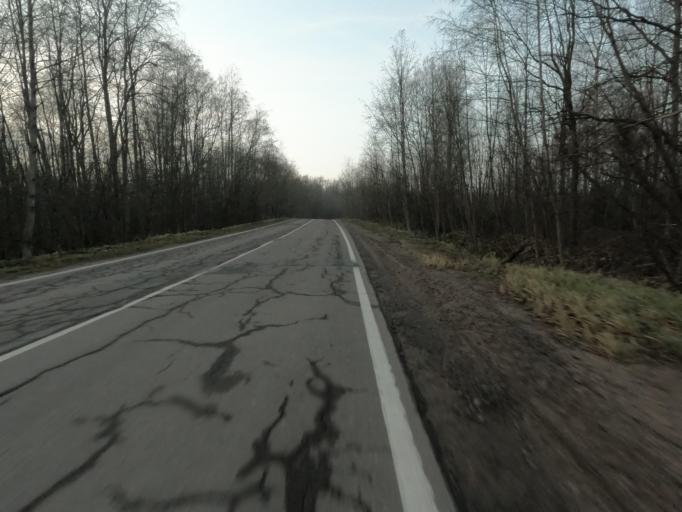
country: RU
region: Leningrad
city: Kirovsk
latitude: 59.8575
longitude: 30.9868
